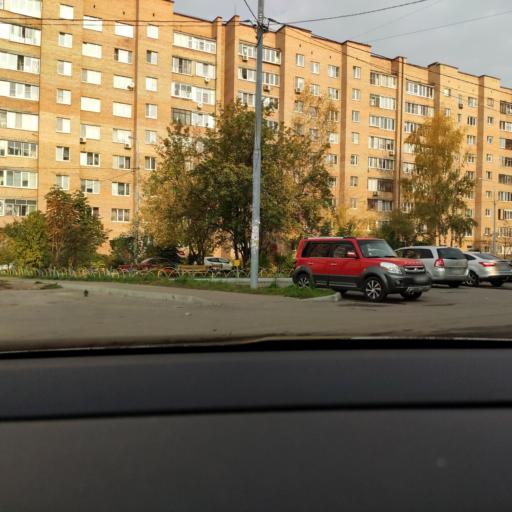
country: RU
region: Moskovskaya
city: Ivanteyevka
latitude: 55.9668
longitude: 37.9114
